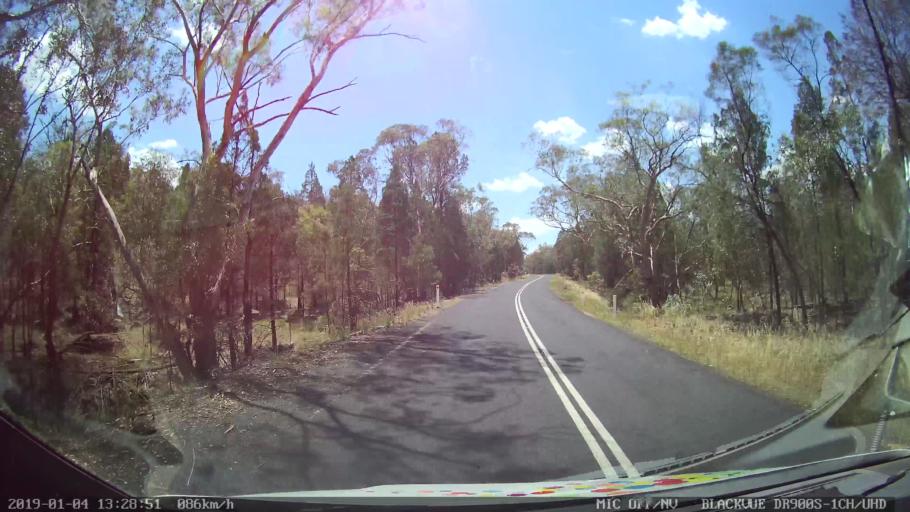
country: AU
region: New South Wales
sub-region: Parkes
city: Peak Hill
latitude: -32.6537
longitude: 148.5495
